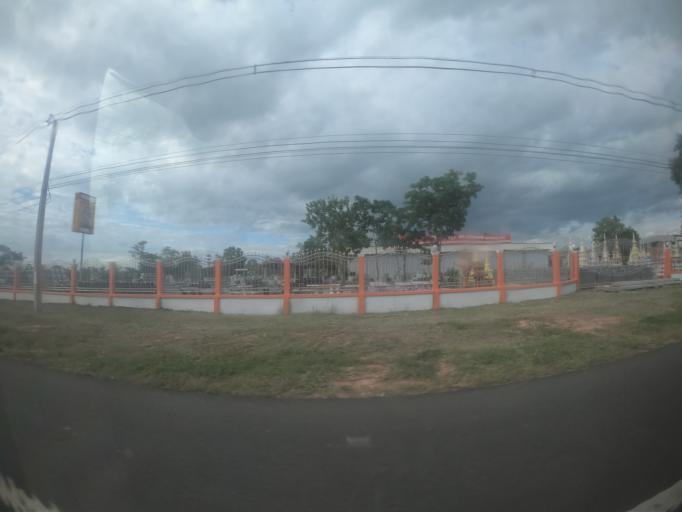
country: TH
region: Surin
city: Kap Choeng
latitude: 14.5367
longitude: 103.5245
